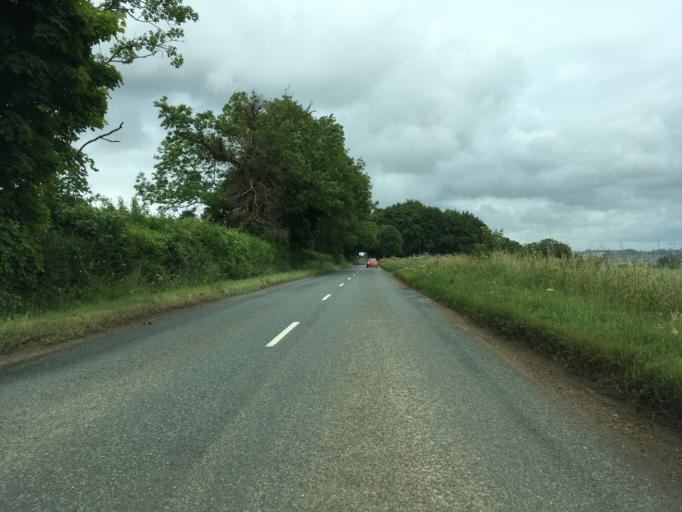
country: GB
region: England
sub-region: Gloucestershire
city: Chipping Campden
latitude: 52.0501
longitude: -1.8030
